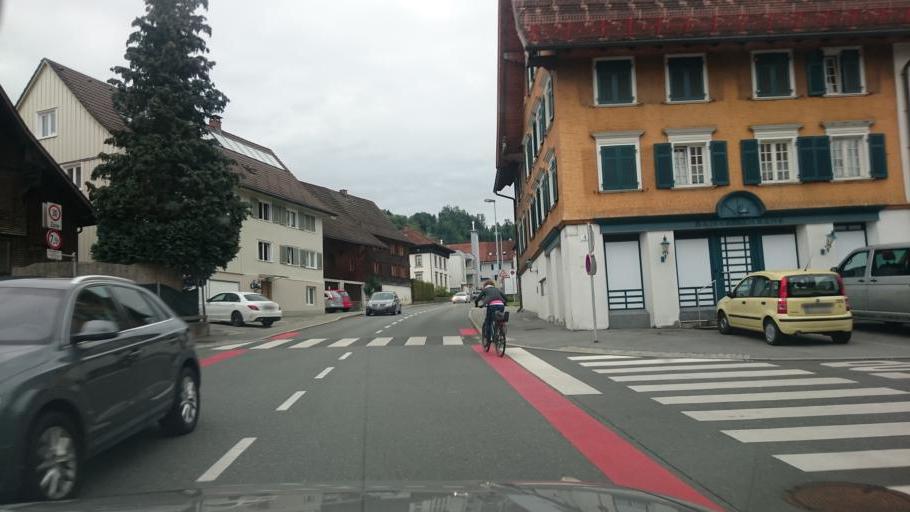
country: AT
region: Vorarlberg
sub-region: Politischer Bezirk Dornbirn
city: Dornbirn
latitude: 47.4107
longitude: 9.7511
